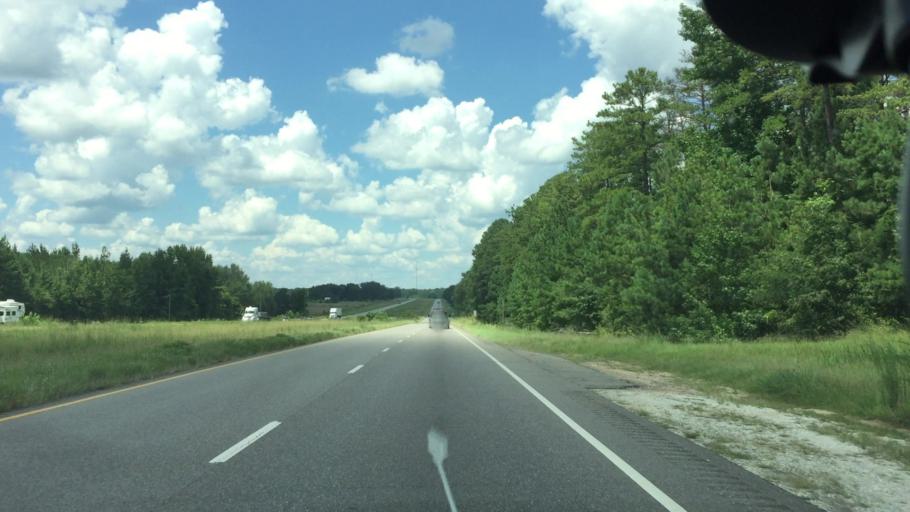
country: US
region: Alabama
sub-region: Montgomery County
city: Taylor
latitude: 32.0222
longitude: -86.0313
